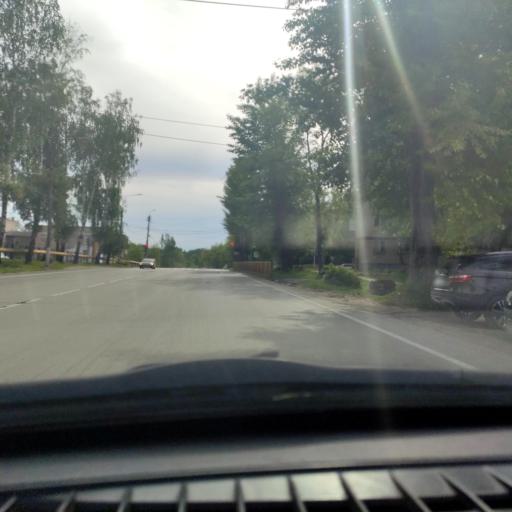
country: RU
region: Samara
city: Zhigulevsk
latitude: 53.4034
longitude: 49.5062
